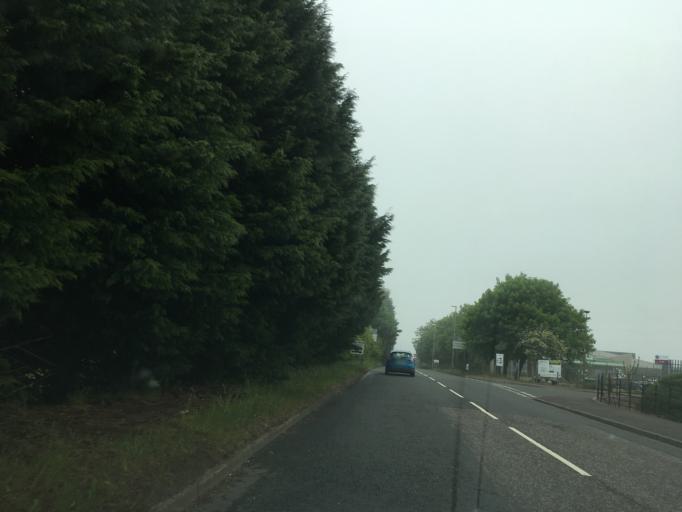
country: GB
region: Scotland
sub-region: Midlothian
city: Penicuik
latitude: 55.8476
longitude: -3.1920
